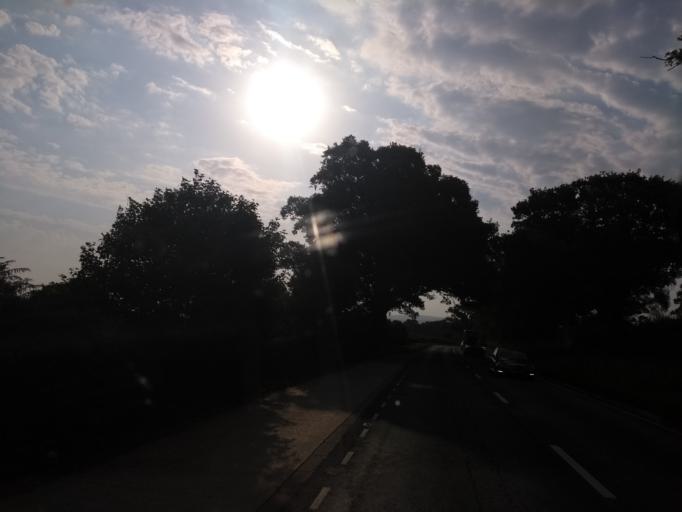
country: GB
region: England
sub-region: Devon
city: Axminster
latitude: 50.7842
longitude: -3.0474
